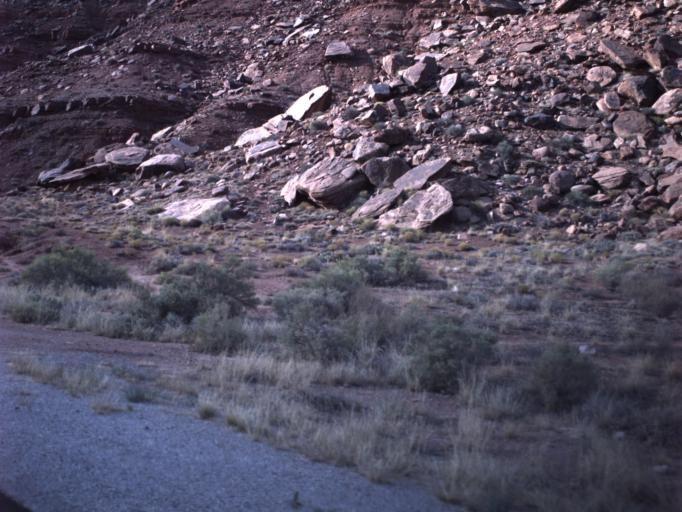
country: US
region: Utah
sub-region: Grand County
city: Moab
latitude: 38.6504
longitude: -109.4818
